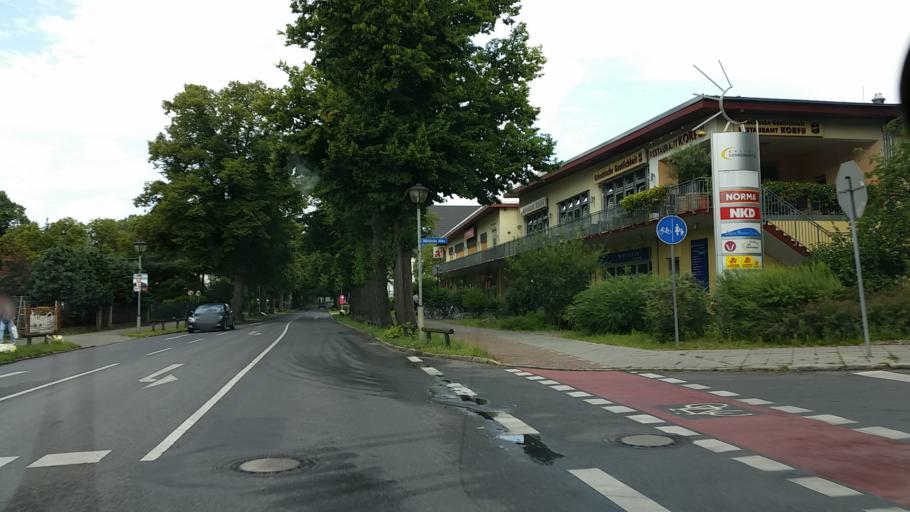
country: DE
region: Brandenburg
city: Glienicke
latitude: 52.6302
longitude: 13.3239
